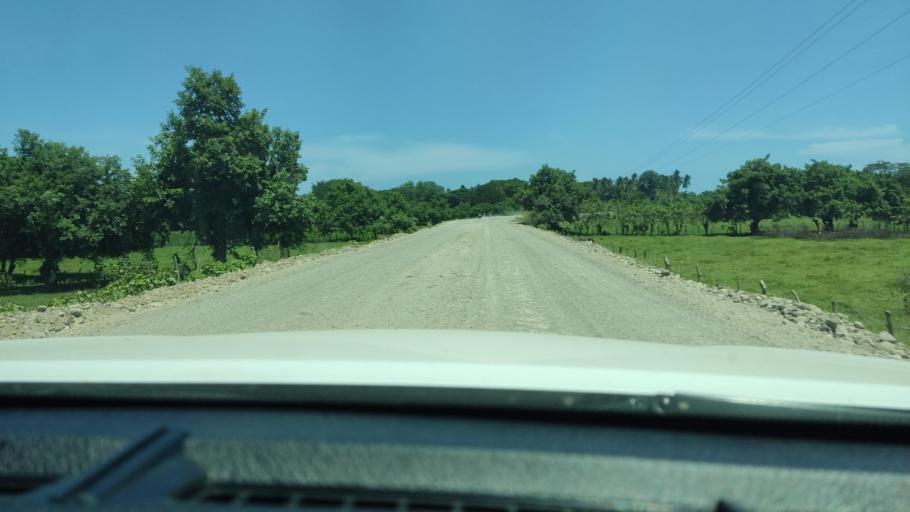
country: SV
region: Ahuachapan
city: San Francisco Menendez
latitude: 13.7946
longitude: -90.1174
